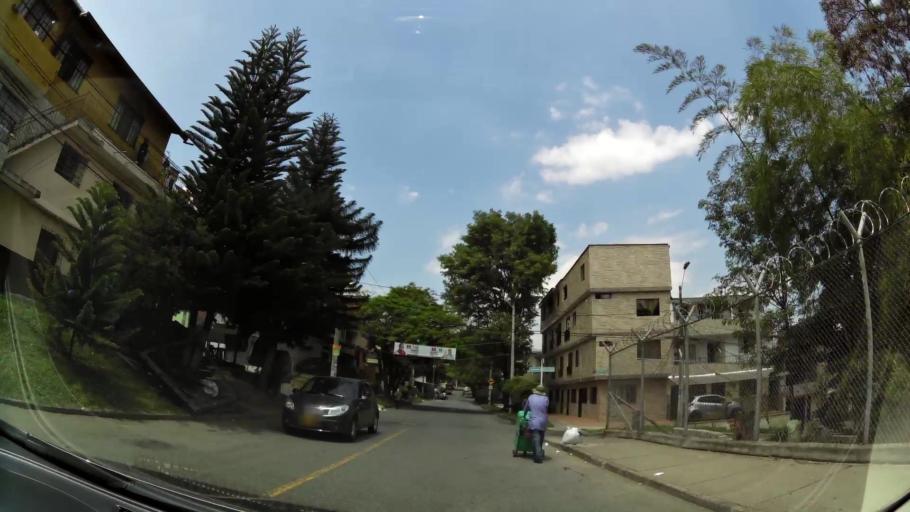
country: CO
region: Antioquia
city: Bello
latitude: 6.3036
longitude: -75.5687
